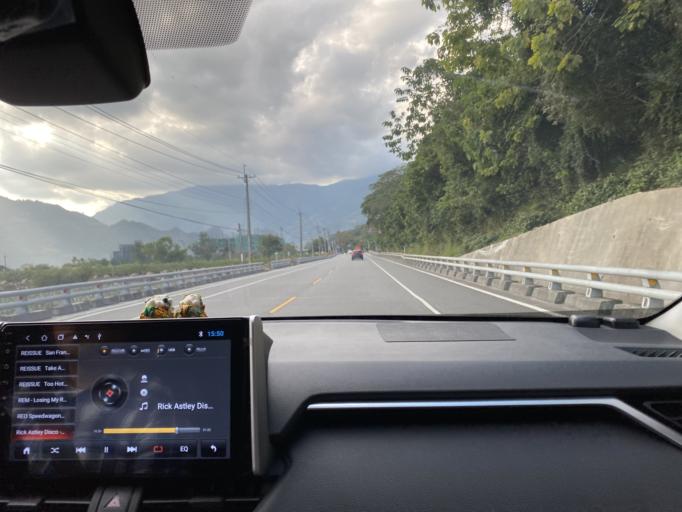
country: TW
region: Taiwan
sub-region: Taitung
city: Taitung
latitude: 22.8976
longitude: 121.1150
